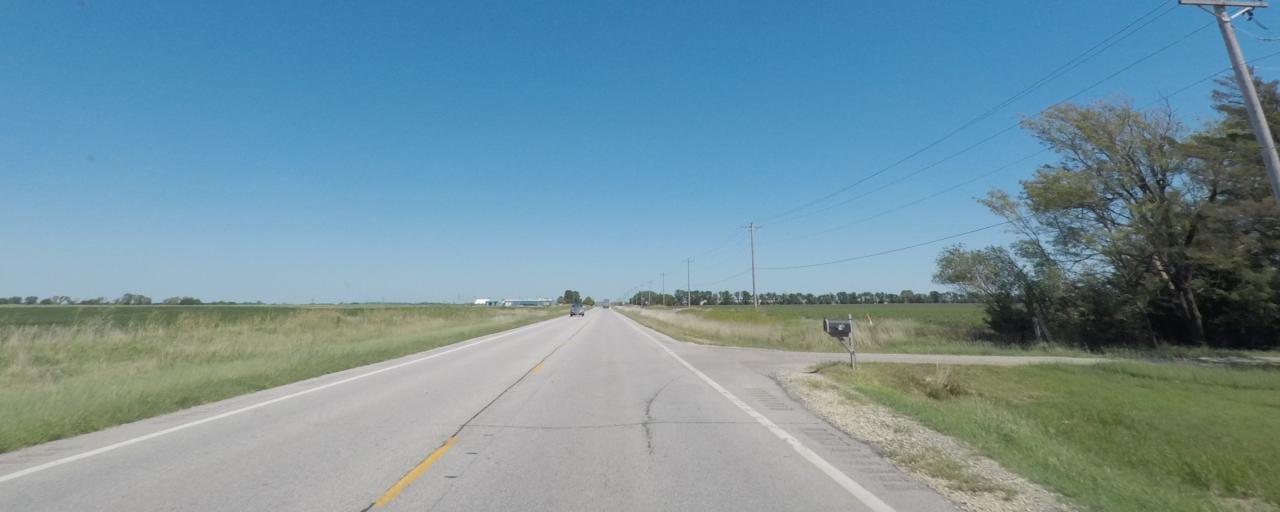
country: US
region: Kansas
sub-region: Sumner County
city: Wellington
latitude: 37.3135
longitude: -97.3847
